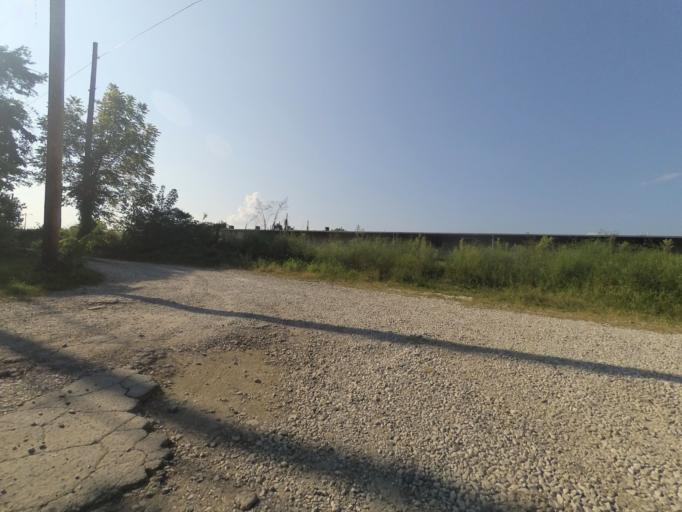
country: US
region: West Virginia
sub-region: Cabell County
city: Huntington
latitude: 38.4138
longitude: -82.4526
